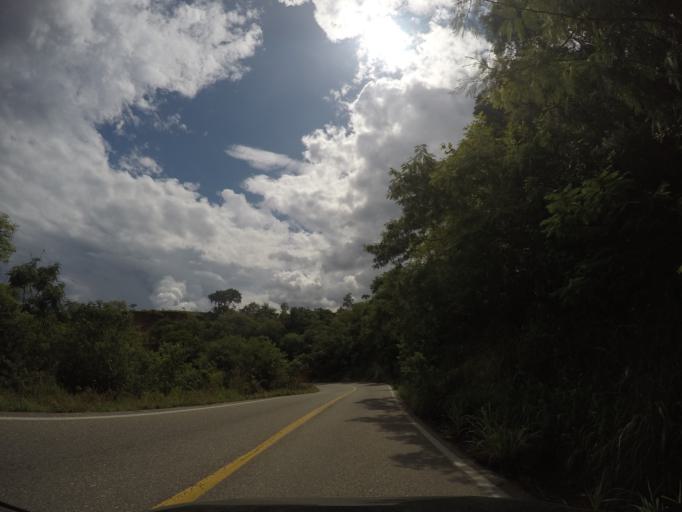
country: MX
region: Oaxaca
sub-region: San Jeronimo Coatlan
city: San Cristobal Honduras
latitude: 16.4348
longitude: -97.0572
